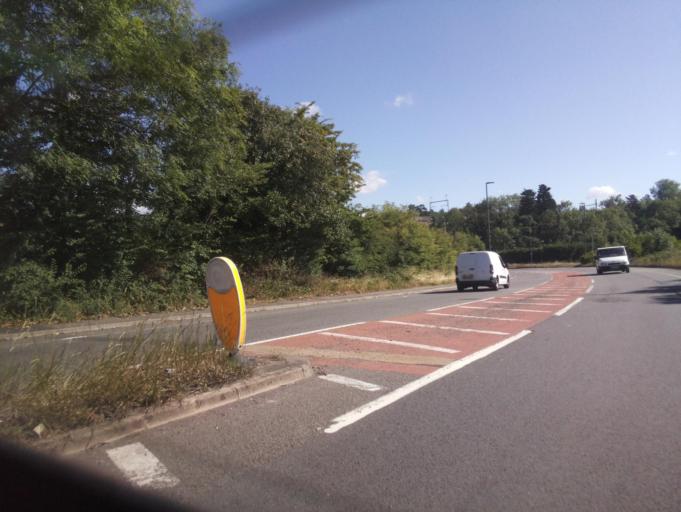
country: GB
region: England
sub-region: South Gloucestershire
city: Winterbourne
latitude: 51.5180
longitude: -2.4800
